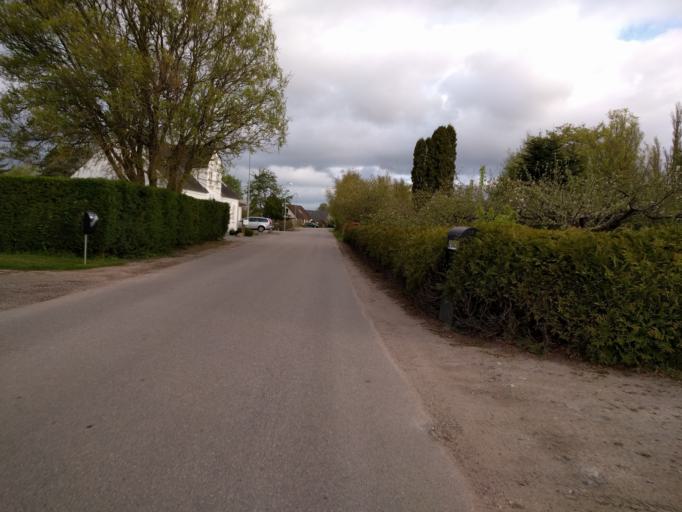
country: DK
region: South Denmark
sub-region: Odense Kommune
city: Bullerup
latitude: 55.4332
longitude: 10.5126
